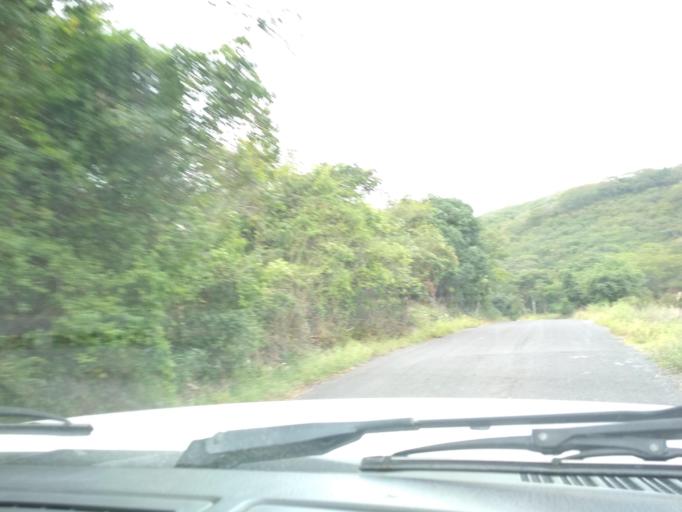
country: MX
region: Veracruz
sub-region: Actopan
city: Trapiche del Rosario
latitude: 19.5675
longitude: -96.7888
